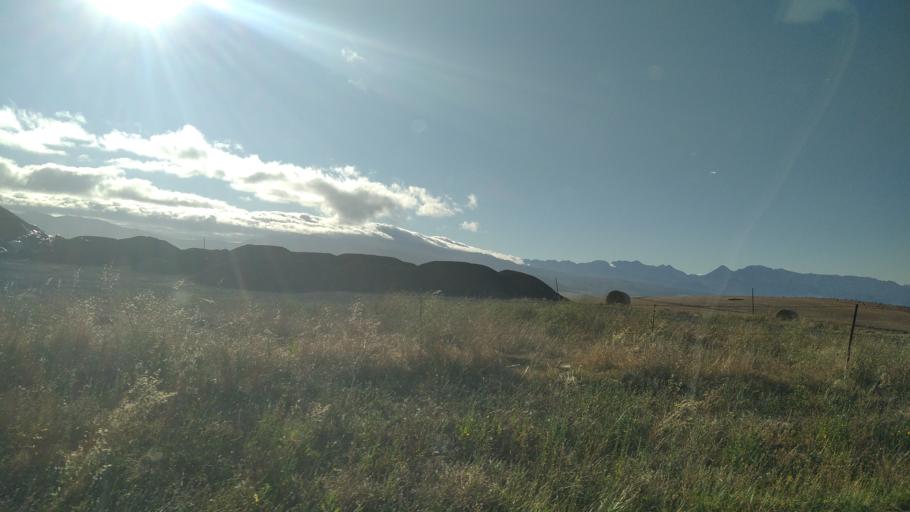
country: ZA
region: Western Cape
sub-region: Overberg District Municipality
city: Caledon
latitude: -34.1493
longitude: 19.3000
